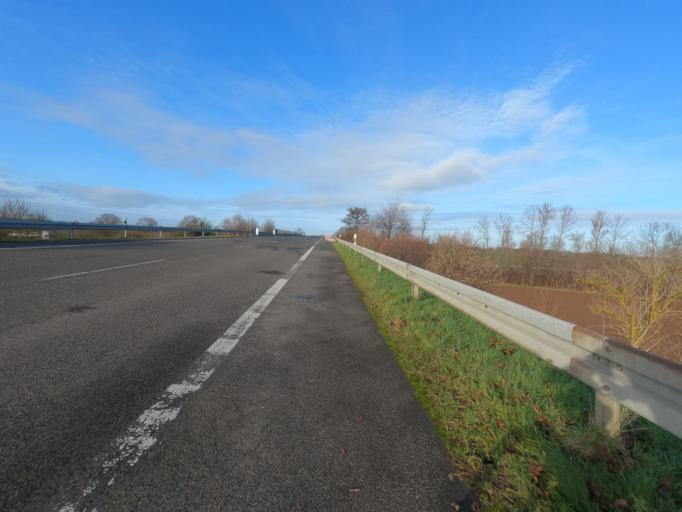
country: DE
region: North Rhine-Westphalia
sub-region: Regierungsbezirk Koln
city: Titz
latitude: 51.0023
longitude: 6.3975
